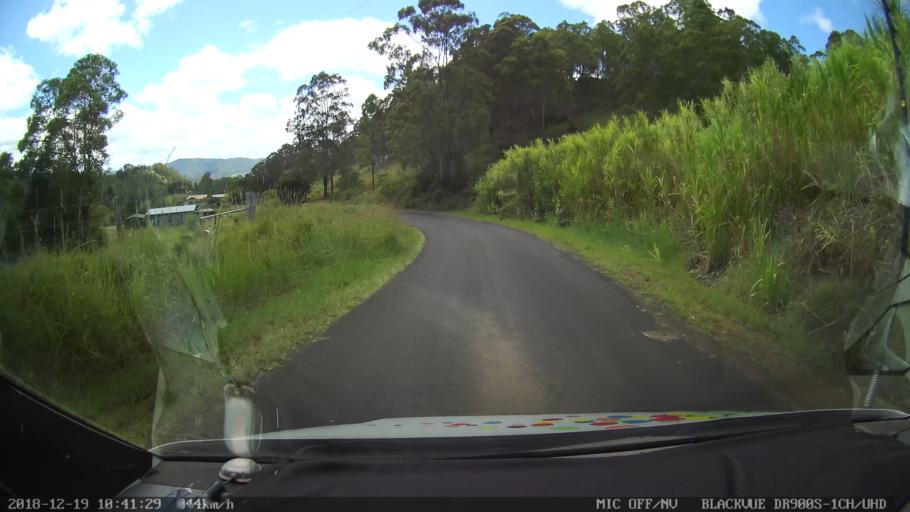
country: AU
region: New South Wales
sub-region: Lismore Municipality
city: Nimbin
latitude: -28.5894
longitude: 153.1617
